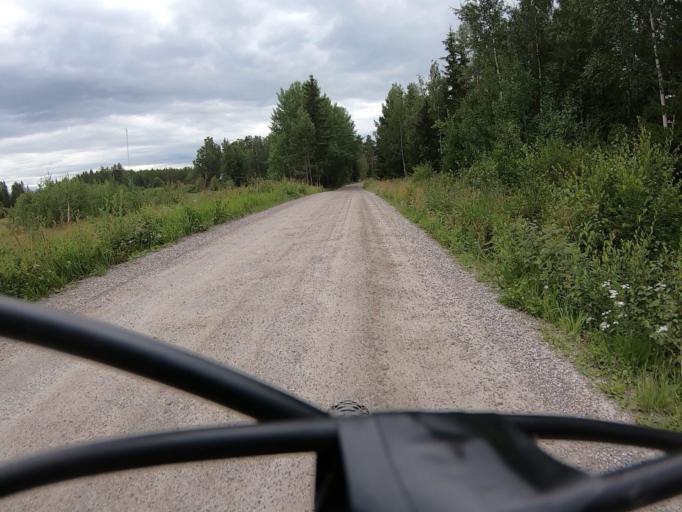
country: FI
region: Varsinais-Suomi
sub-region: Vakka-Suomi
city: Uusikaupunki
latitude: 60.8418
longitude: 21.3867
